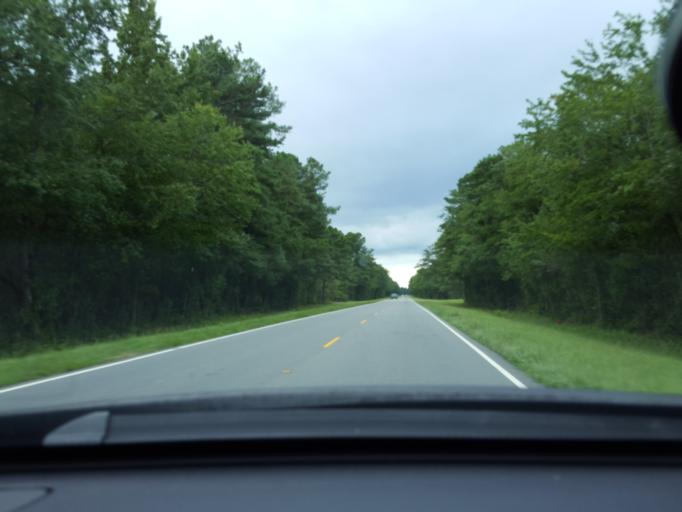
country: US
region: North Carolina
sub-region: Bladen County
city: Elizabethtown
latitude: 34.7307
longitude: -78.4365
